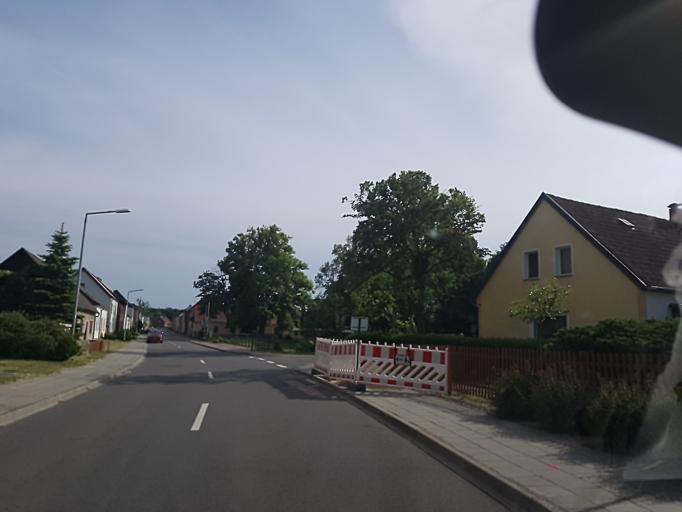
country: DE
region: Saxony-Anhalt
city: Kropstadt
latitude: 51.9642
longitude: 12.7460
